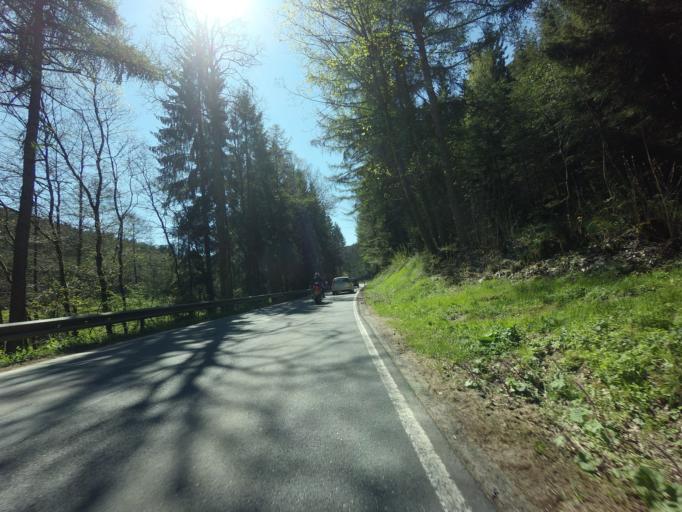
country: DE
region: North Rhine-Westphalia
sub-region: Regierungsbezirk Arnsberg
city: Kirchhundem
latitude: 51.0880
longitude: 8.1438
